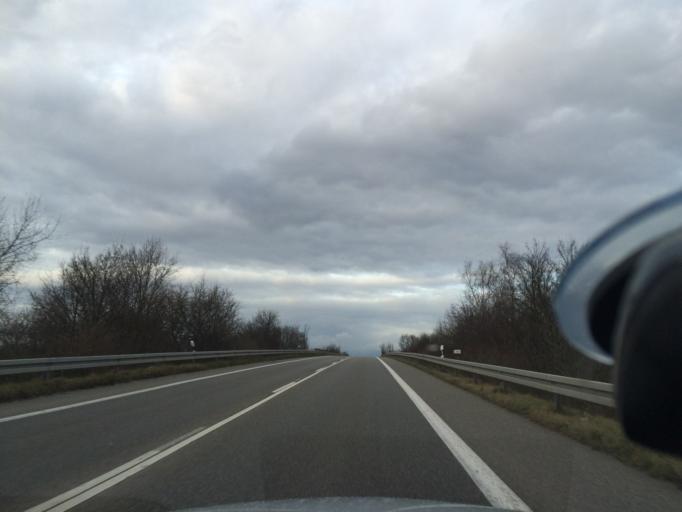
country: DE
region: Hesse
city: Weiterstadt
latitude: 49.9148
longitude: 8.6109
